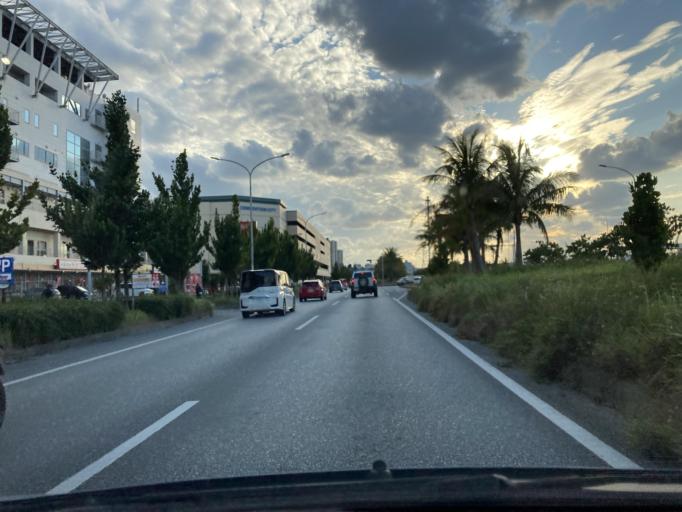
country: JP
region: Okinawa
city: Ginowan
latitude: 26.2767
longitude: 127.7312
